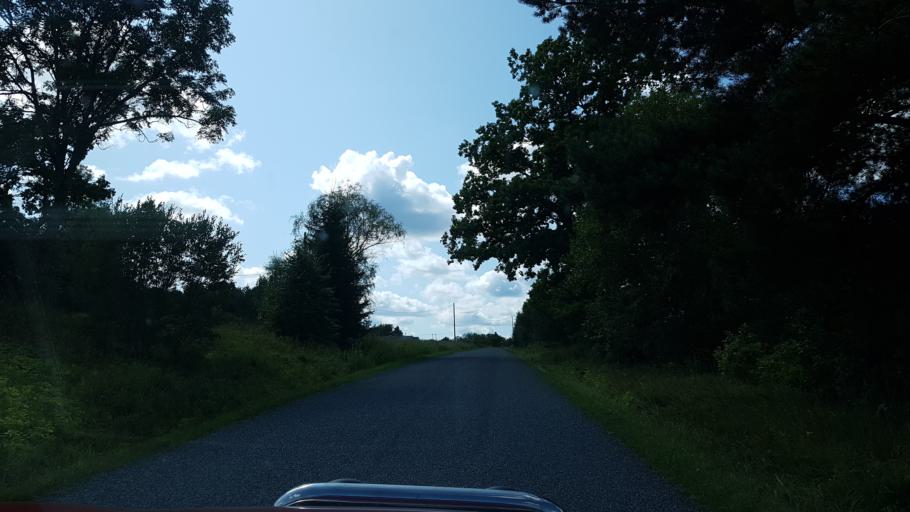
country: EE
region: Vorumaa
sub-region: Voru linn
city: Voru
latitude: 57.7274
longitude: 27.2668
